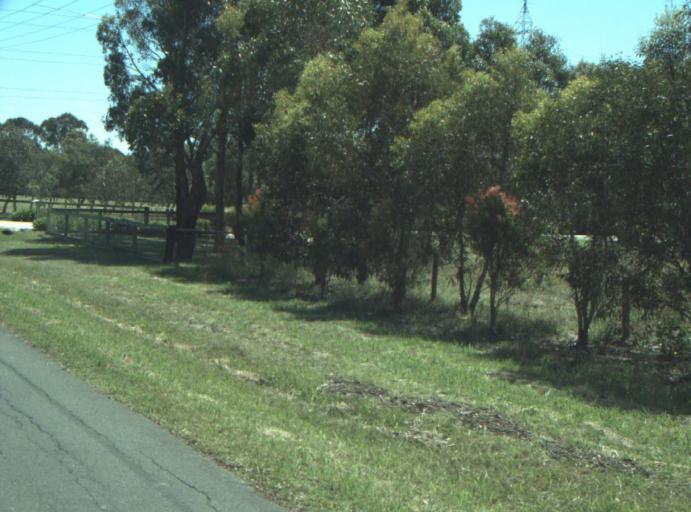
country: AU
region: Victoria
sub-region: Greater Geelong
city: Breakwater
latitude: -38.2020
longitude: 144.3618
